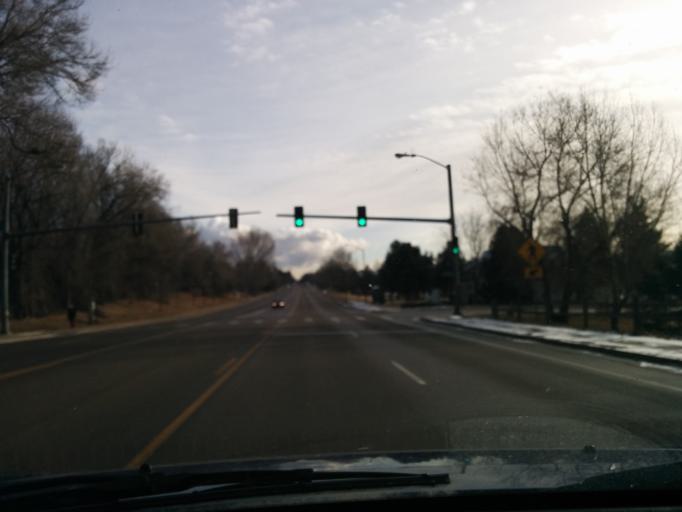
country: US
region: Colorado
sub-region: Larimer County
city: Fort Collins
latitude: 40.5673
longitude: -105.1028
